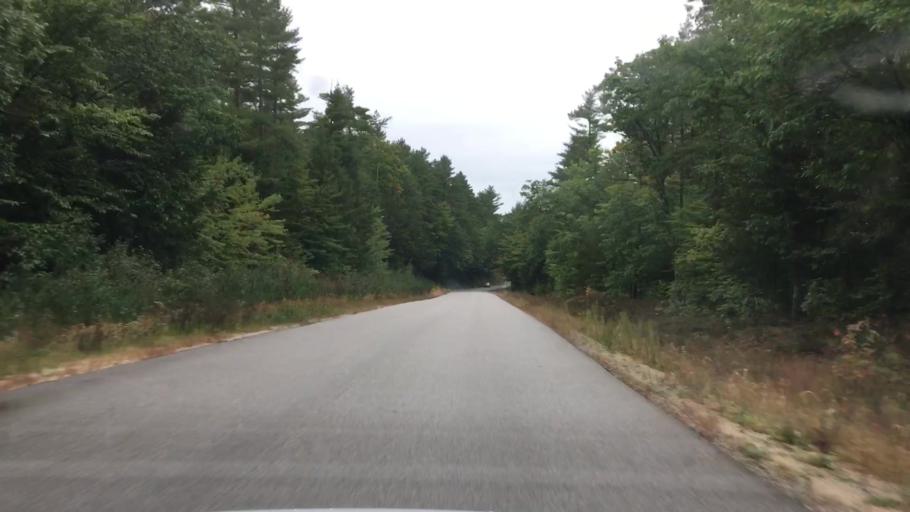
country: US
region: Maine
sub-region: Cumberland County
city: Harrison
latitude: 44.0295
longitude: -70.5961
